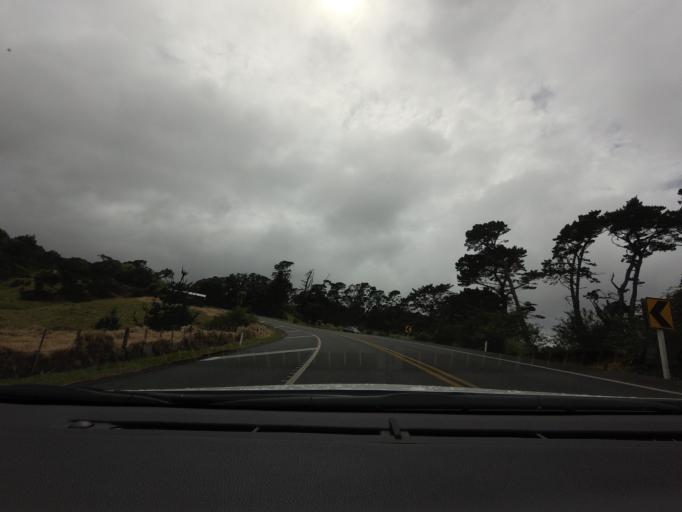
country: NZ
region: Auckland
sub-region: Auckland
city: Warkworth
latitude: -36.5558
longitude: 174.7065
